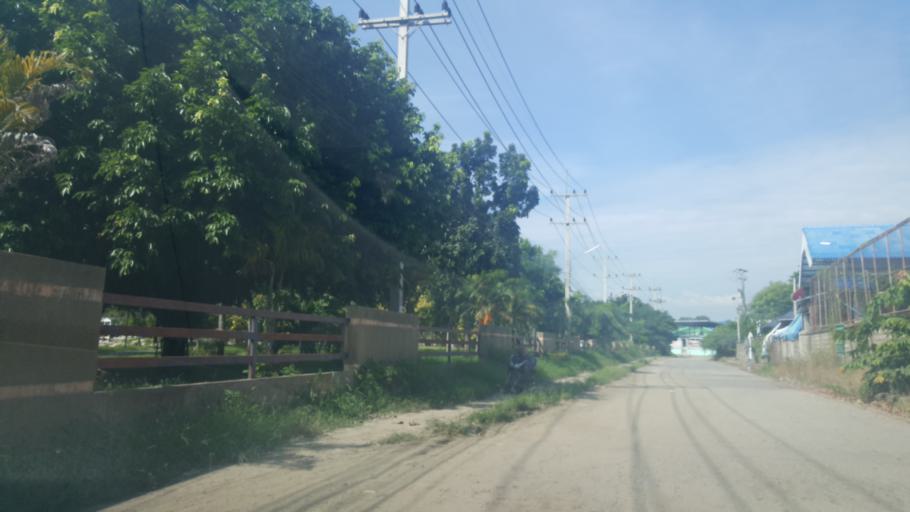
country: TH
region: Chon Buri
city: Sattahip
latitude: 12.6715
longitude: 100.8983
